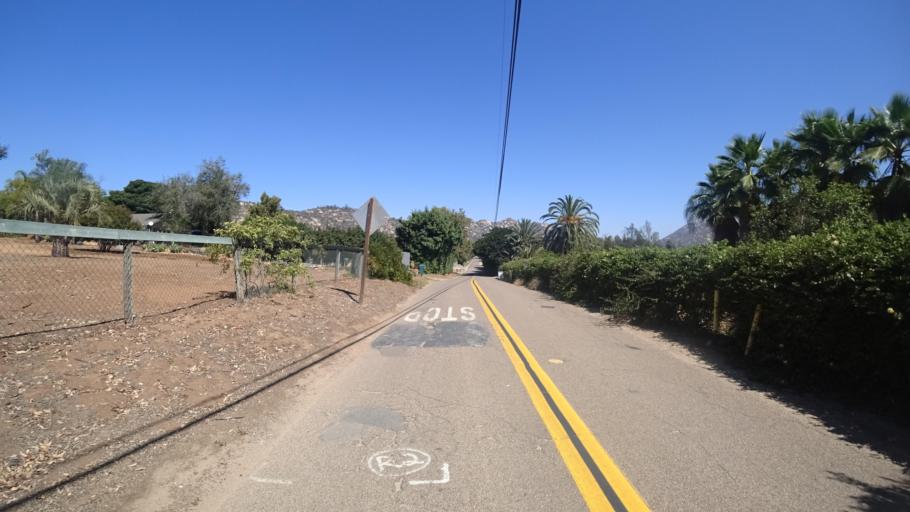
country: US
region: California
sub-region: San Diego County
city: Rainbow
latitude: 33.4106
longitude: -117.1519
